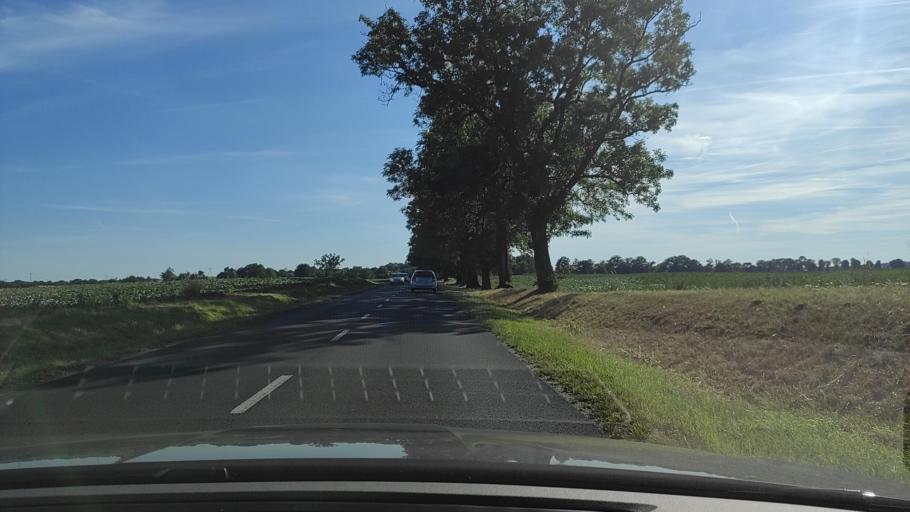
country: PL
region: Greater Poland Voivodeship
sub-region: Powiat poznanski
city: Kobylnica
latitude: 52.5007
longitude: 17.1122
